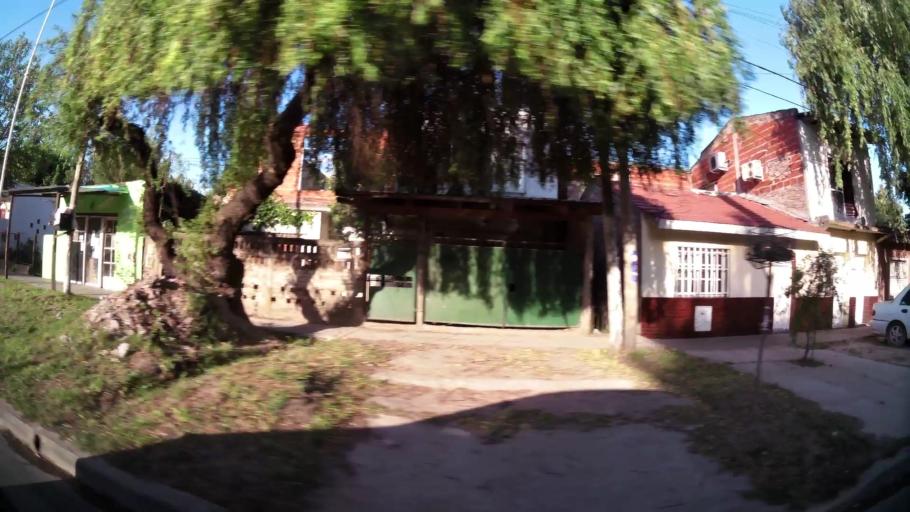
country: AR
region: Buenos Aires
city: Santa Catalina - Dique Lujan
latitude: -34.4734
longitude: -58.7506
